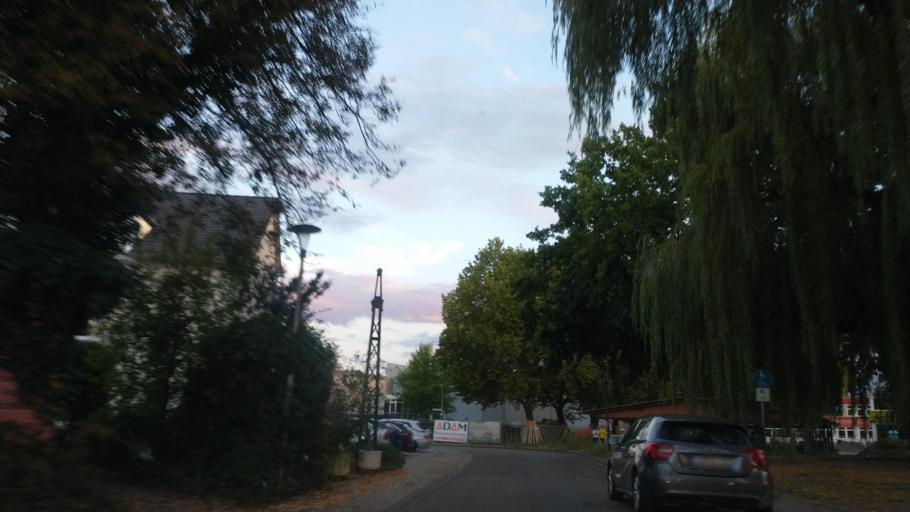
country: DE
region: Baden-Wuerttemberg
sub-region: Freiburg Region
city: Willstatt
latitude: 48.5398
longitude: 7.8955
